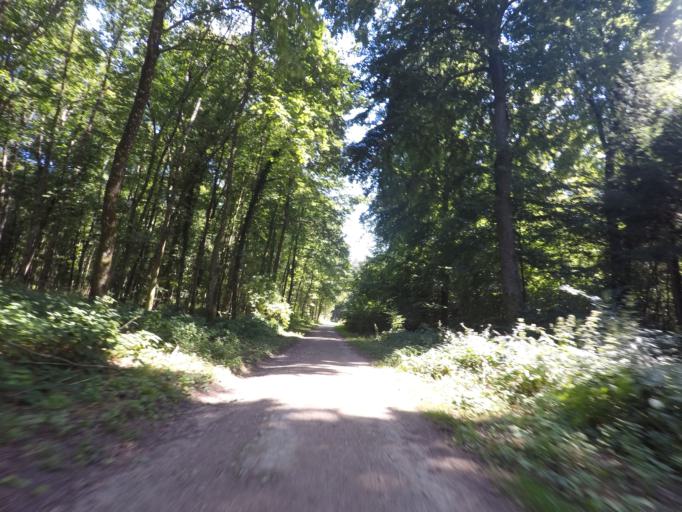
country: LU
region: Luxembourg
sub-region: Canton de Luxembourg
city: Strassen
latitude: 49.6315
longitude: 6.0802
